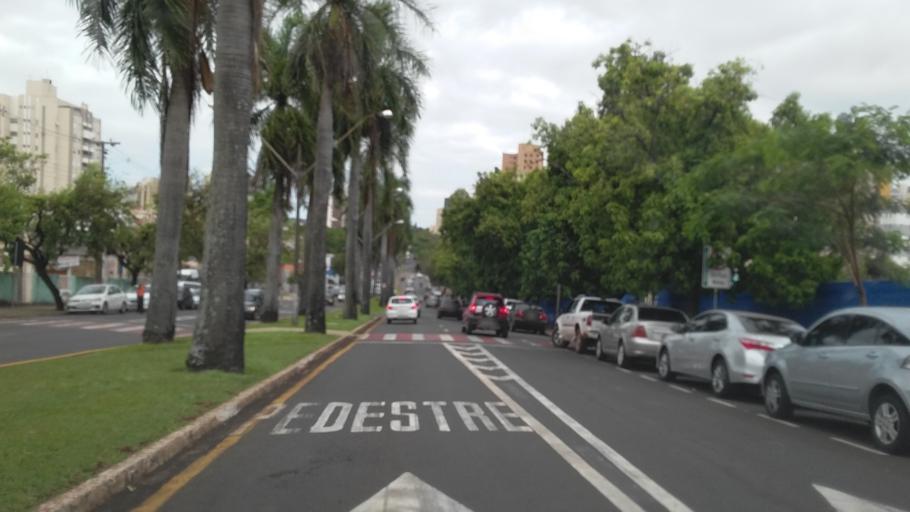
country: BR
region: Parana
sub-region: Londrina
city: Londrina
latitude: -23.3198
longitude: -51.1598
